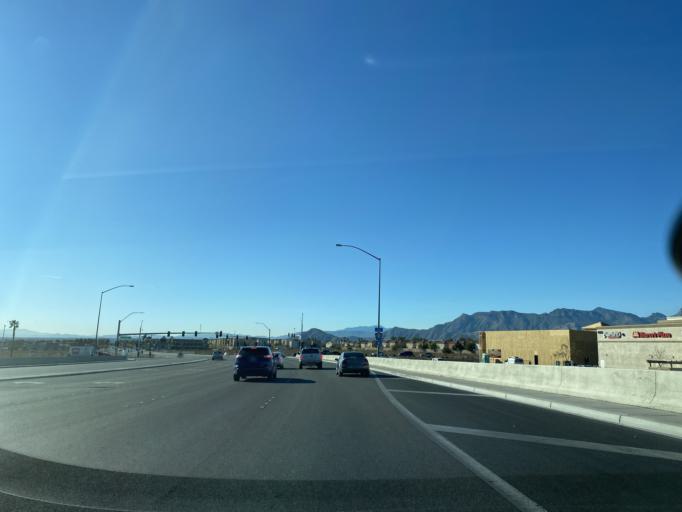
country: US
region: Nevada
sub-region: Clark County
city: Summerlin South
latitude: 36.2965
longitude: -115.2877
